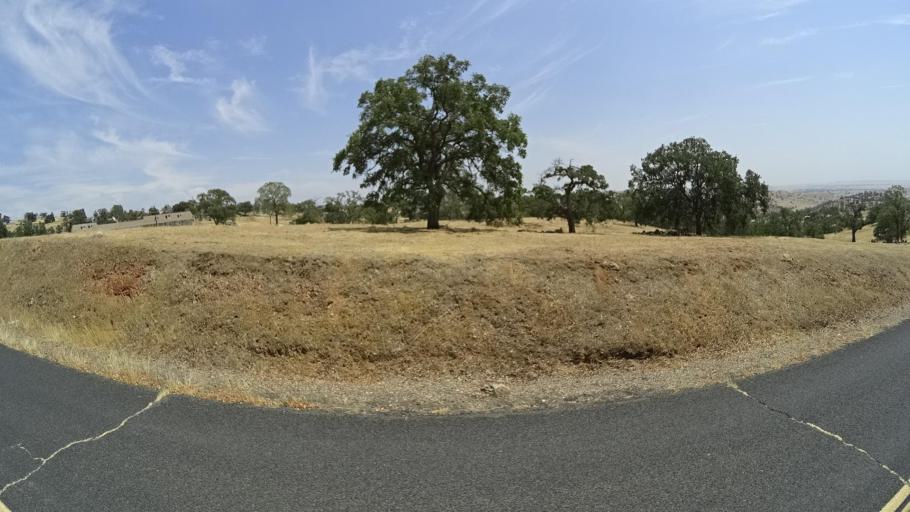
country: US
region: California
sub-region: Tuolumne County
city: Jamestown
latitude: 37.6519
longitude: -120.3526
